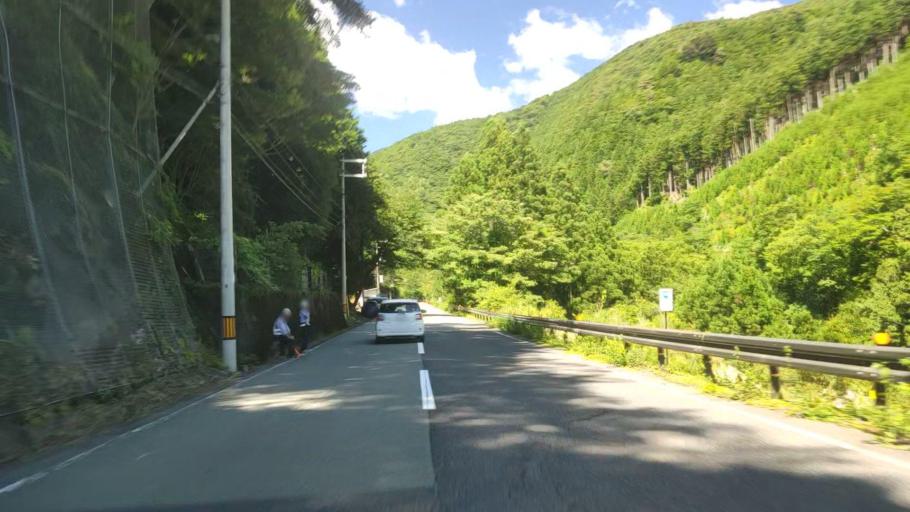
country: JP
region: Mie
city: Owase
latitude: 34.1703
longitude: 136.0013
